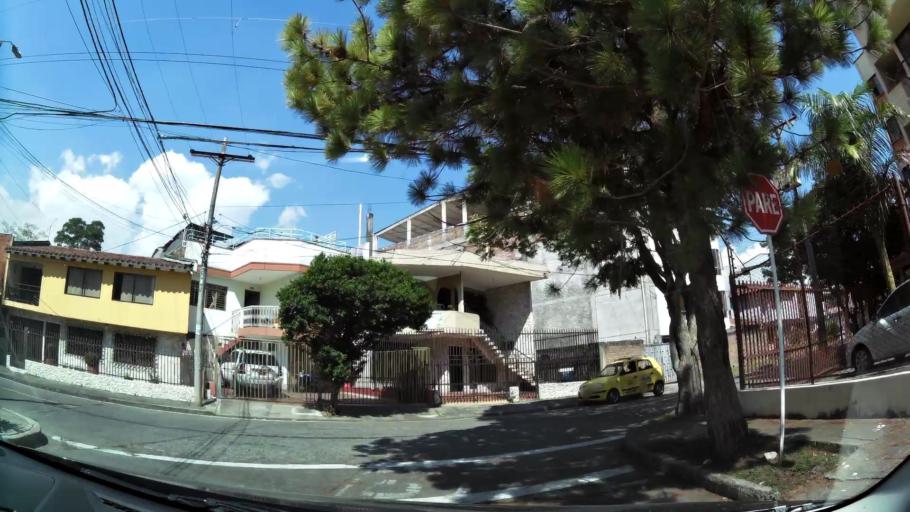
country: CO
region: Valle del Cauca
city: Cali
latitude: 3.4290
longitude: -76.5293
